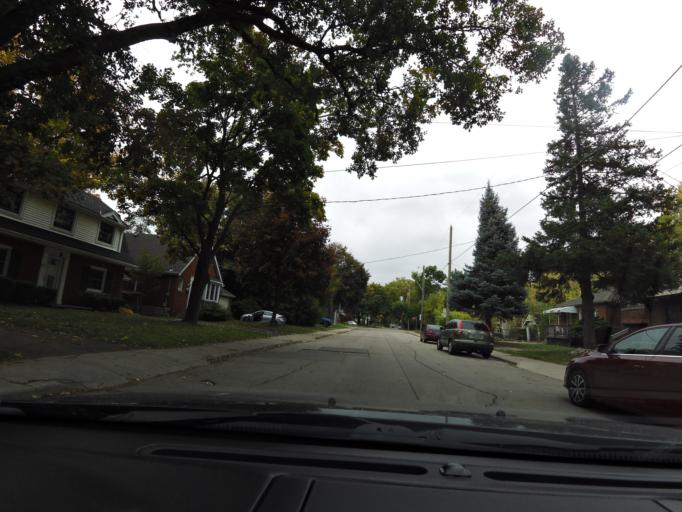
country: CA
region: Ontario
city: Hamilton
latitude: 43.2571
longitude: -79.9141
